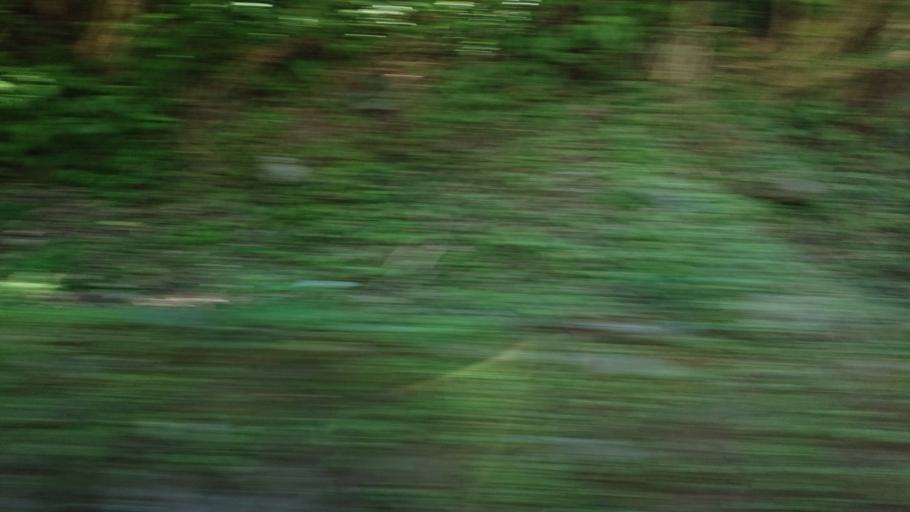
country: TW
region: Taiwan
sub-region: Yilan
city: Yilan
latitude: 24.5773
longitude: 121.4820
